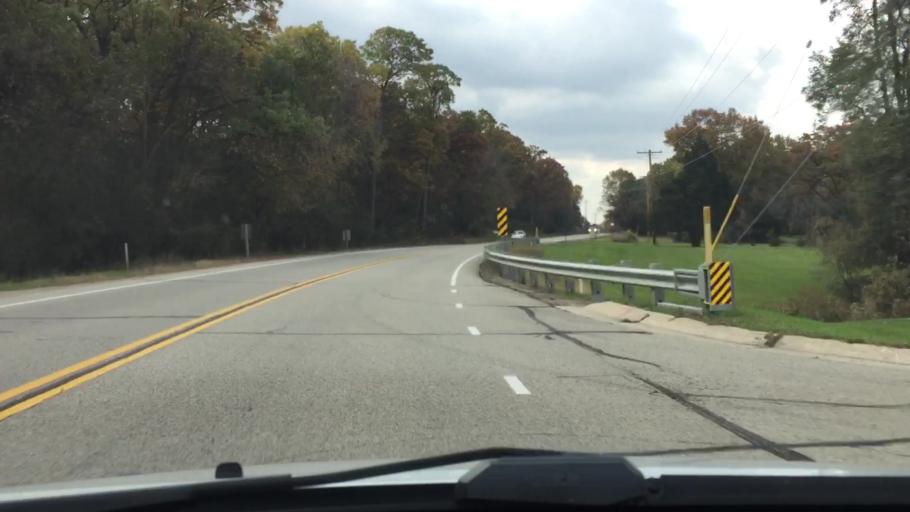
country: US
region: Wisconsin
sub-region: Waukesha County
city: Dousman
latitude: 42.9658
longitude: -88.4739
